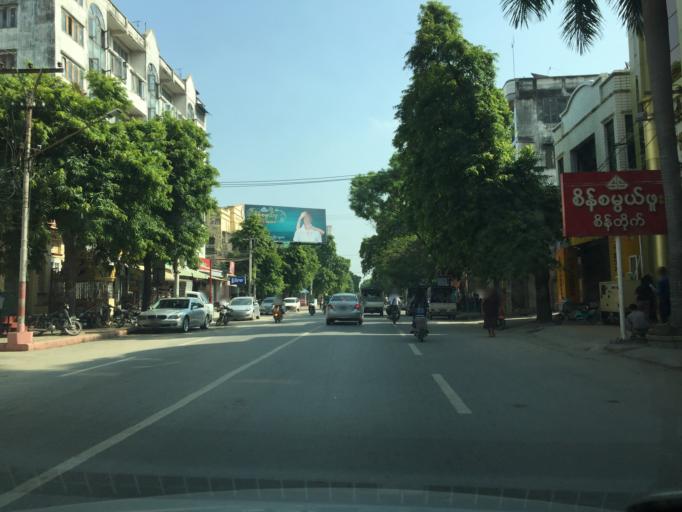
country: MM
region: Mandalay
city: Mandalay
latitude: 21.9751
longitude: 96.0773
